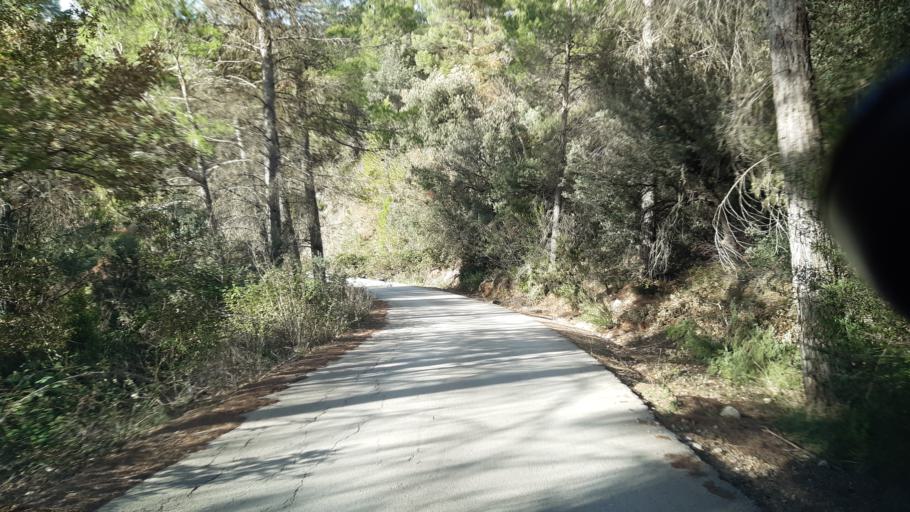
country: ES
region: Aragon
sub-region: Provincia de Teruel
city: Valderrobres
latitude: 40.8484
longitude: 0.2126
